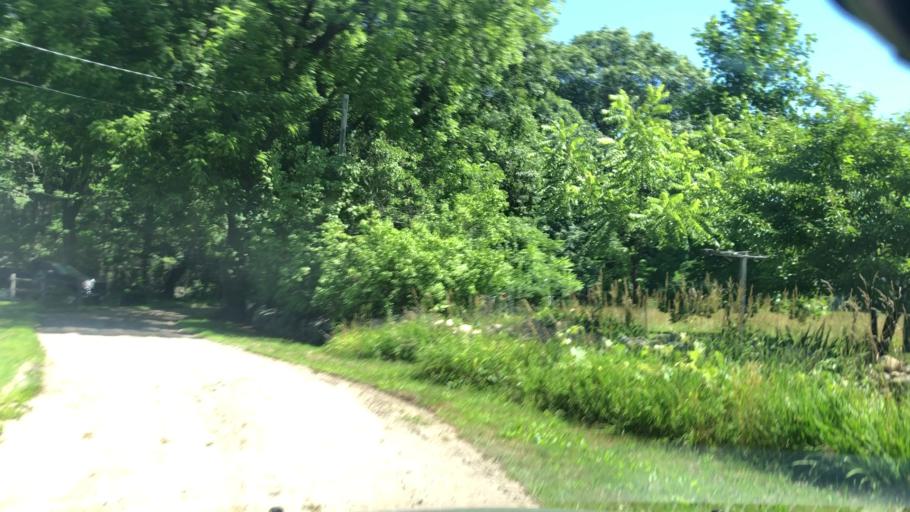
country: US
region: New Hampshire
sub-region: Hillsborough County
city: Milford
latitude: 42.8581
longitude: -71.5828
